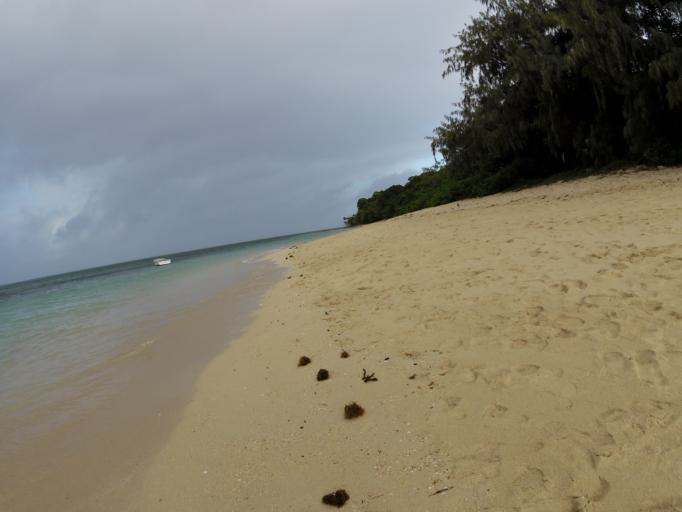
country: AU
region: Queensland
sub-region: Cairns
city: Yorkeys Knob
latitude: -16.7580
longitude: 145.9738
